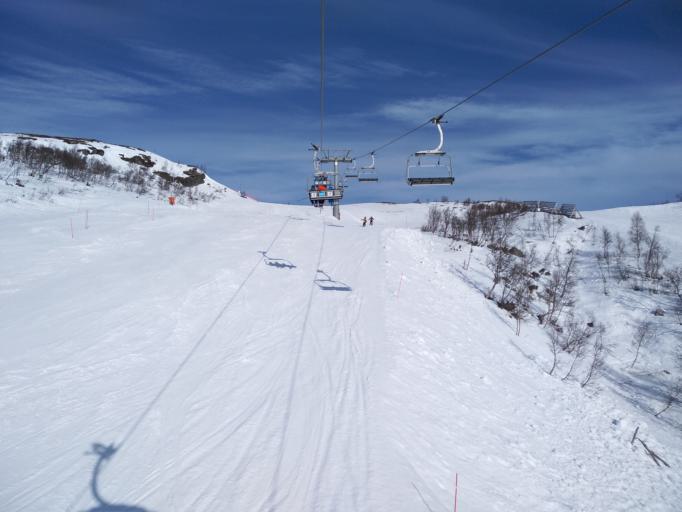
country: NO
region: Aust-Agder
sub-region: Bykle
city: Hovden
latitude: 59.5756
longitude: 7.3149
